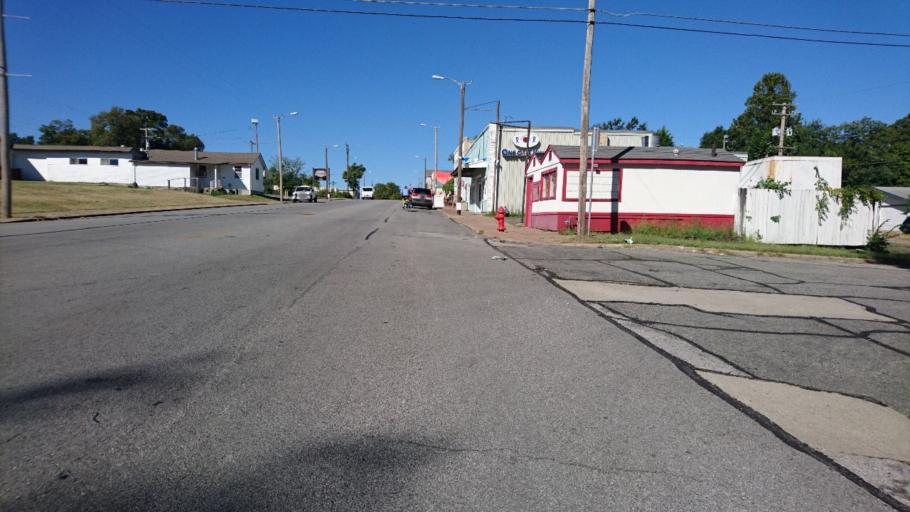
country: US
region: Missouri
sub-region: Jasper County
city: Joplin
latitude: 37.0919
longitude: -94.5048
